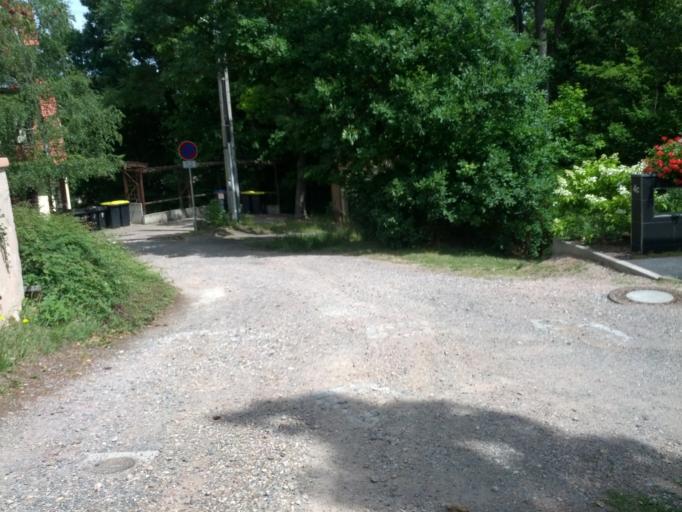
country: DE
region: Thuringia
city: Eisenach
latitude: 50.9622
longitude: 10.3217
